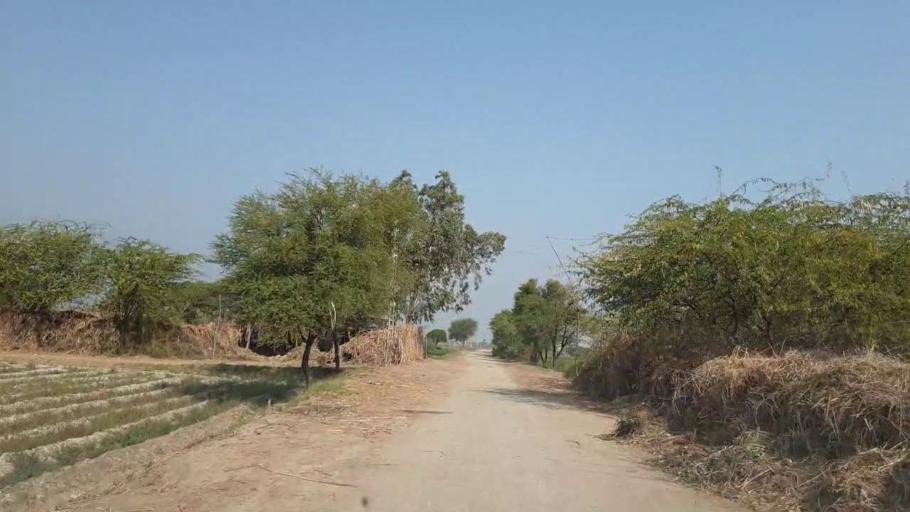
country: PK
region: Sindh
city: Mirpur Khas
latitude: 25.5898
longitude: 69.0149
